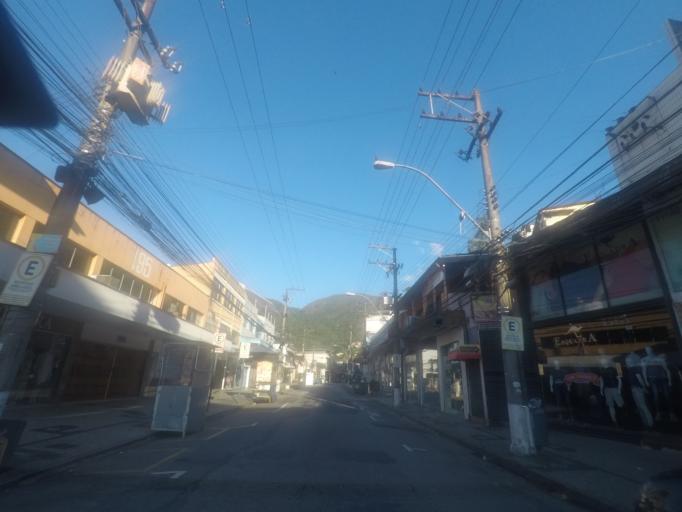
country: BR
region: Rio de Janeiro
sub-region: Petropolis
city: Petropolis
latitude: -22.5151
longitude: -43.1739
